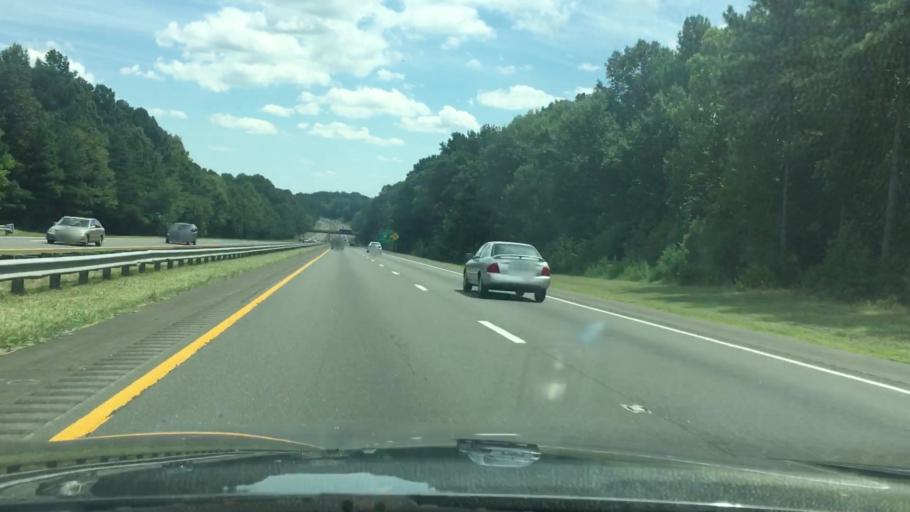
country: US
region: North Carolina
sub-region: Orange County
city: Hillsborough
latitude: 36.0432
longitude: -79.0367
